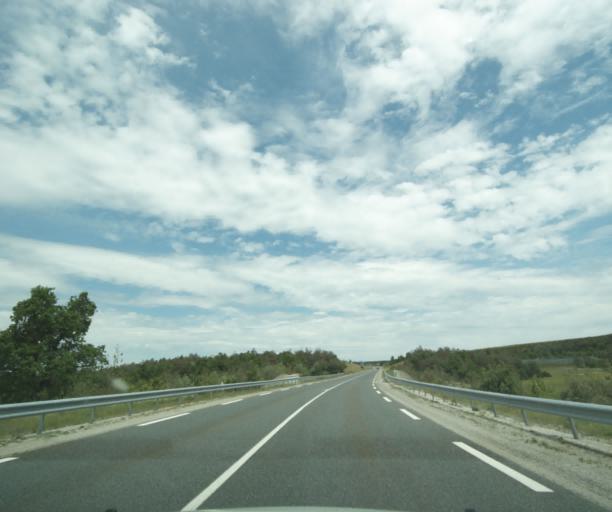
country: FR
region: Midi-Pyrenees
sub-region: Departement de l'Aveyron
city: Creissels
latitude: 44.0251
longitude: 3.0627
